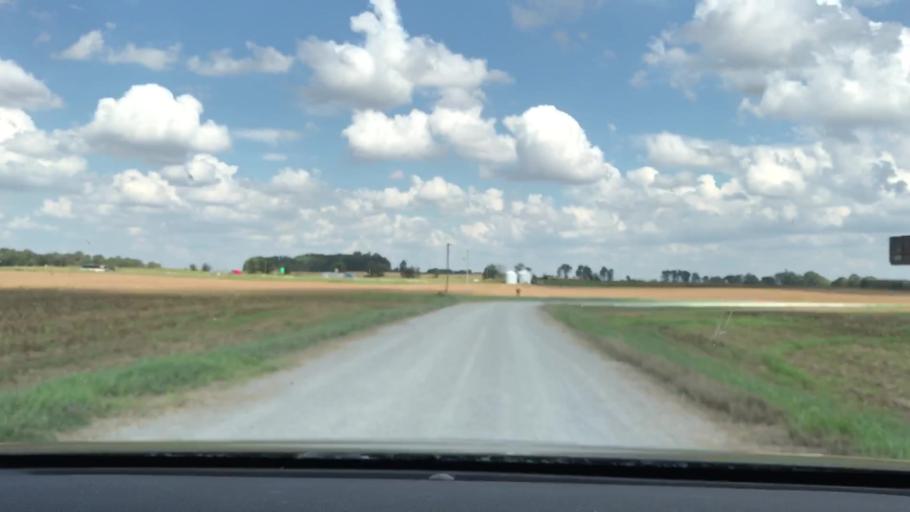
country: US
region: Kentucky
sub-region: Christian County
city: Oak Grove
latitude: 36.6843
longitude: -87.4205
